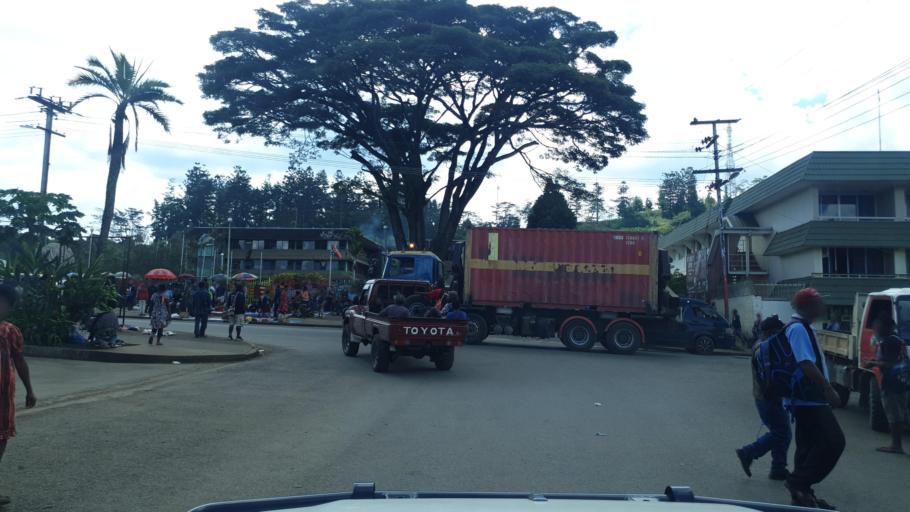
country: PG
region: Eastern Highlands
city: Goroka
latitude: -6.0732
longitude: 145.3944
